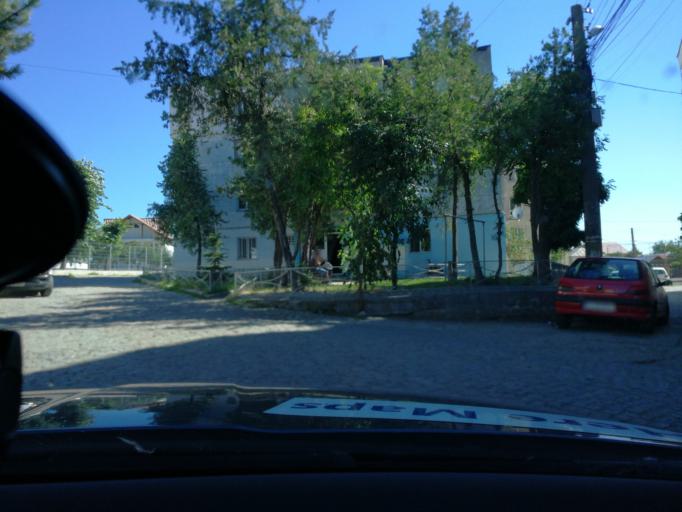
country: RO
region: Tulcea
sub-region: Oras Macin
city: Macin
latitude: 45.2443
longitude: 28.1321
